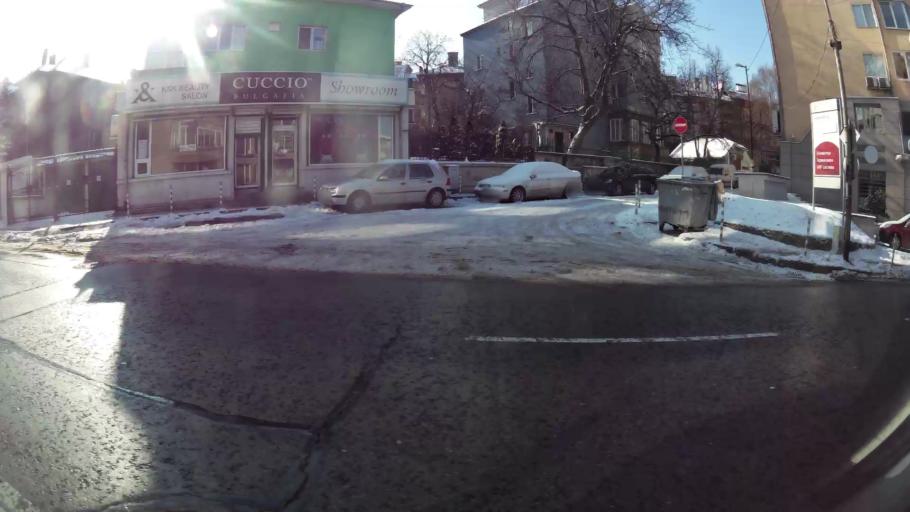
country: BG
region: Sofia-Capital
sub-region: Stolichna Obshtina
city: Sofia
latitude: 42.6771
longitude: 23.3323
